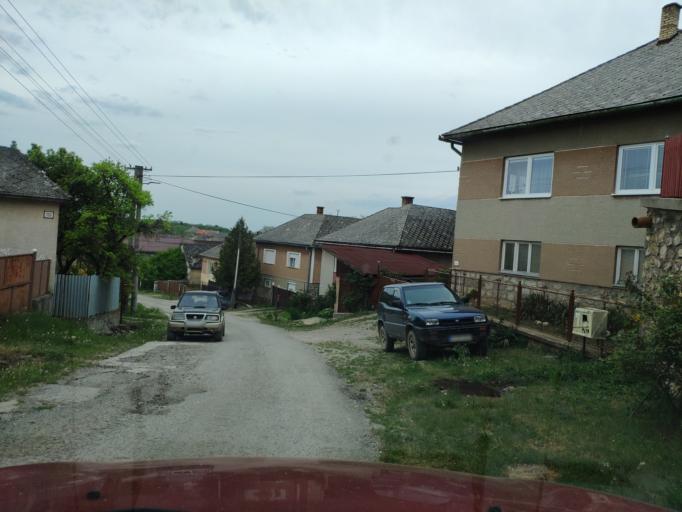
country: SK
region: Kosicky
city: Roznava
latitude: 48.5556
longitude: 20.5201
